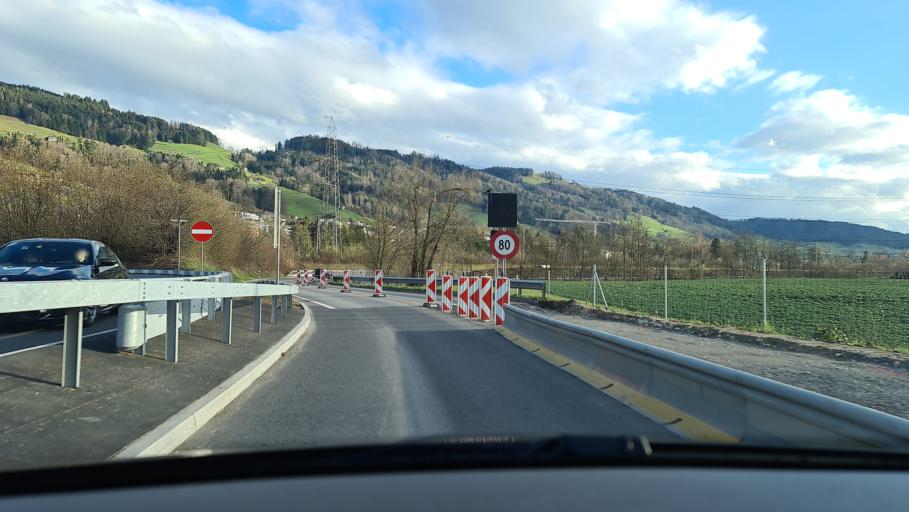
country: CH
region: Lucerne
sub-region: Lucerne-Land District
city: Root
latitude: 47.1246
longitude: 8.3923
